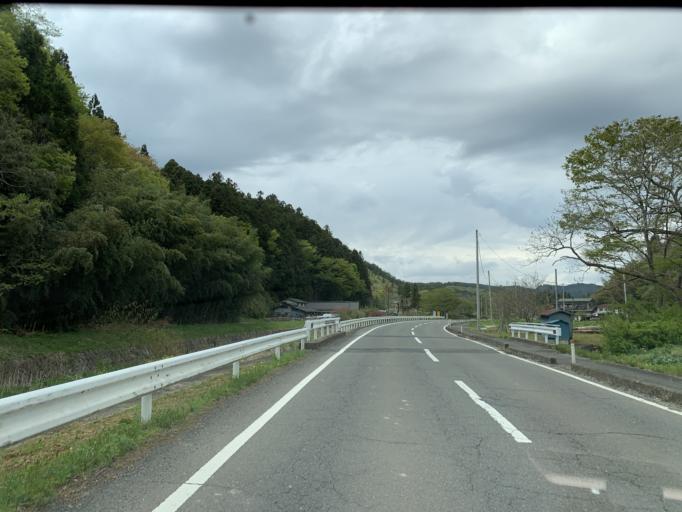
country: JP
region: Iwate
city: Ichinoseki
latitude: 38.7823
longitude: 141.3268
